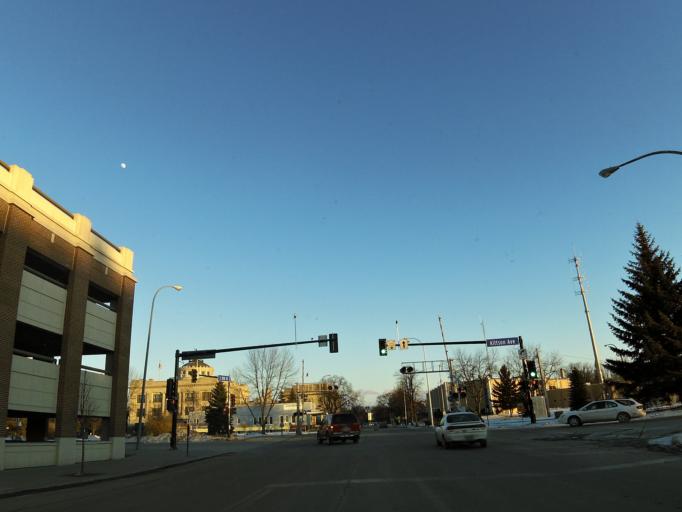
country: US
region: North Dakota
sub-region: Grand Forks County
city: Grand Forks
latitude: 47.9233
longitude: -97.0319
